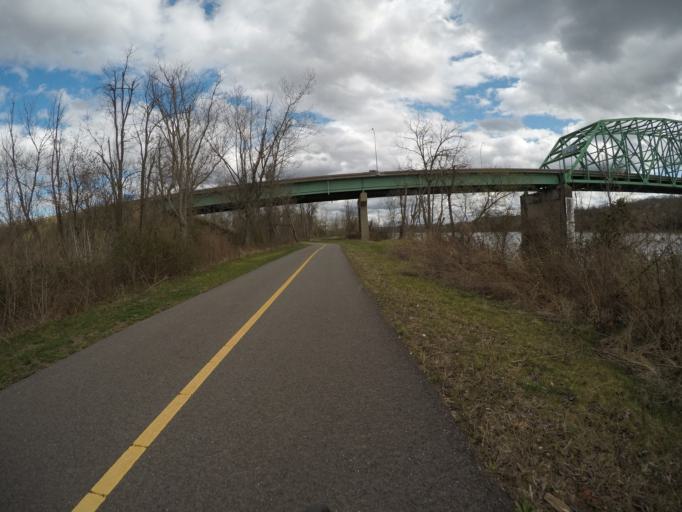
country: US
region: West Virginia
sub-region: Wood County
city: Williamstown
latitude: 39.4064
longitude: -81.4290
